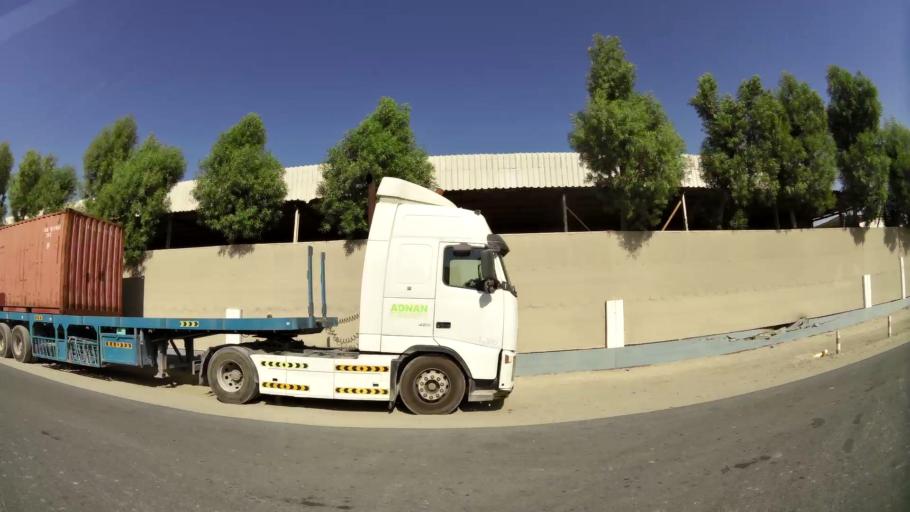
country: AE
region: Dubai
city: Dubai
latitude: 24.9949
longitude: 55.1043
